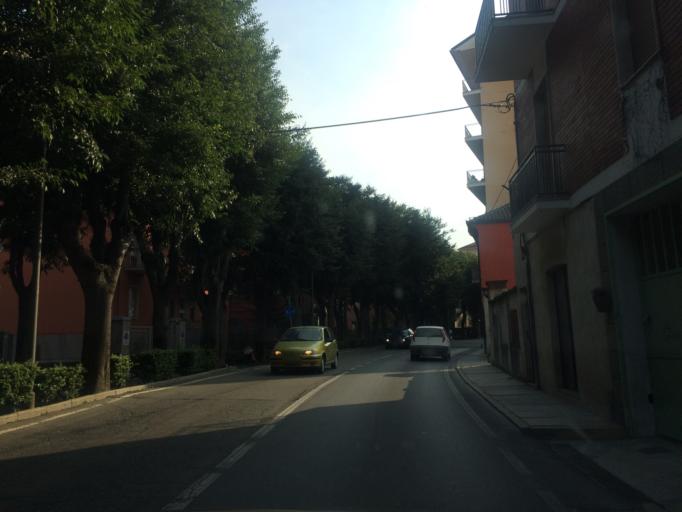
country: IT
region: Piedmont
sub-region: Provincia di Cuneo
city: Alba
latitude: 44.6977
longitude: 8.0381
